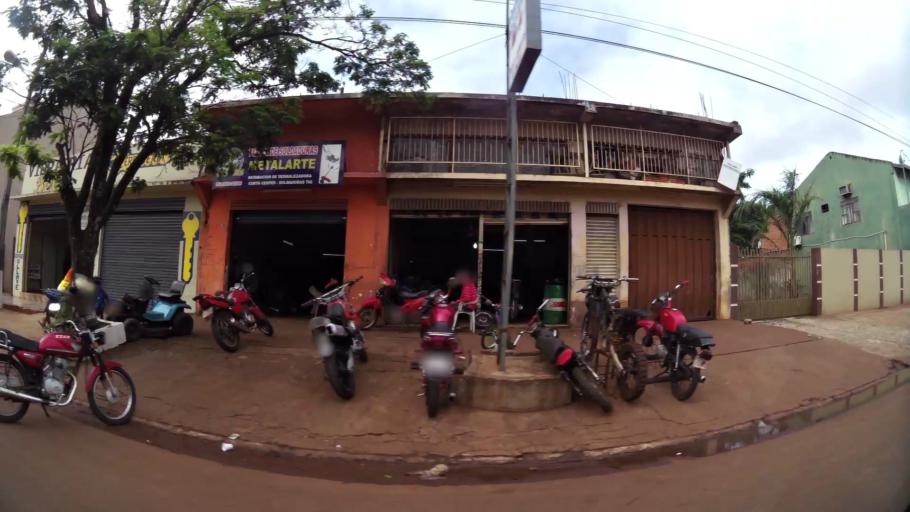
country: PY
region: Alto Parana
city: Ciudad del Este
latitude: -25.3940
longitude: -54.6408
